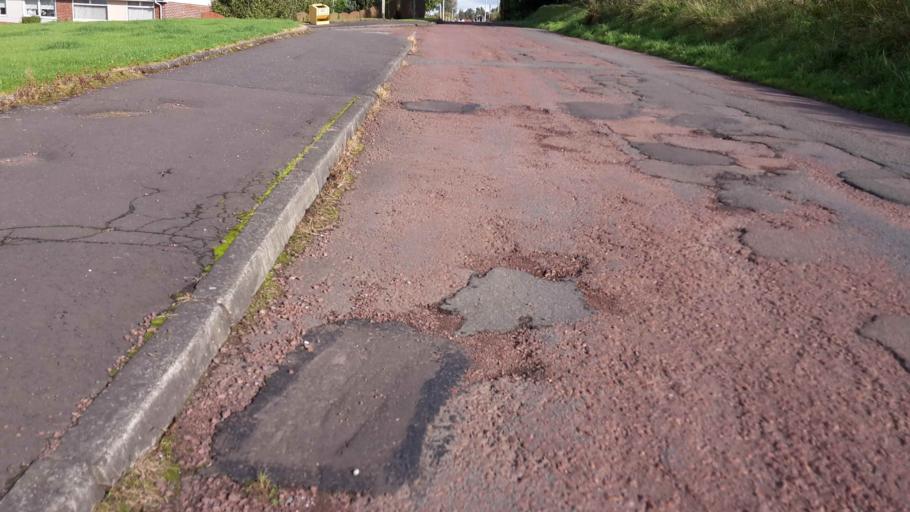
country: GB
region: Scotland
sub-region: South Lanarkshire
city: Carluke
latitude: 55.7260
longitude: -3.8363
